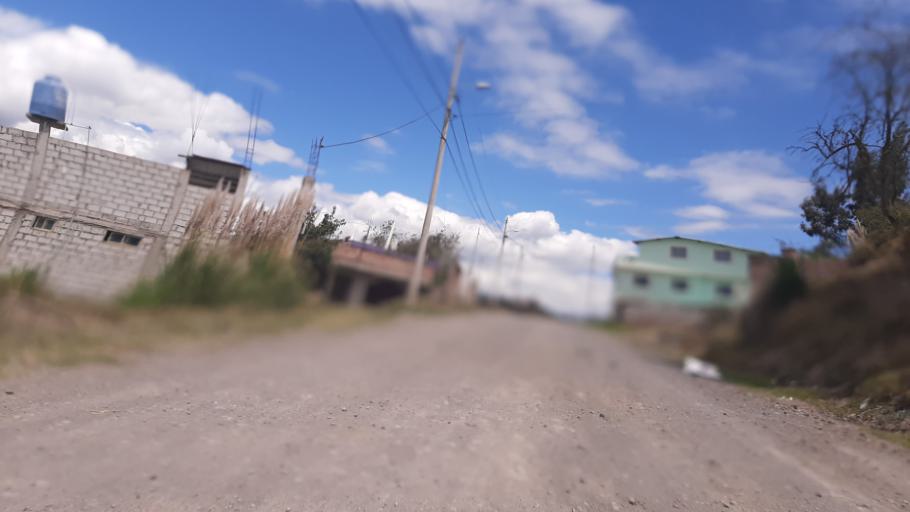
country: EC
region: Chimborazo
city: Riobamba
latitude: -1.6495
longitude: -78.6364
